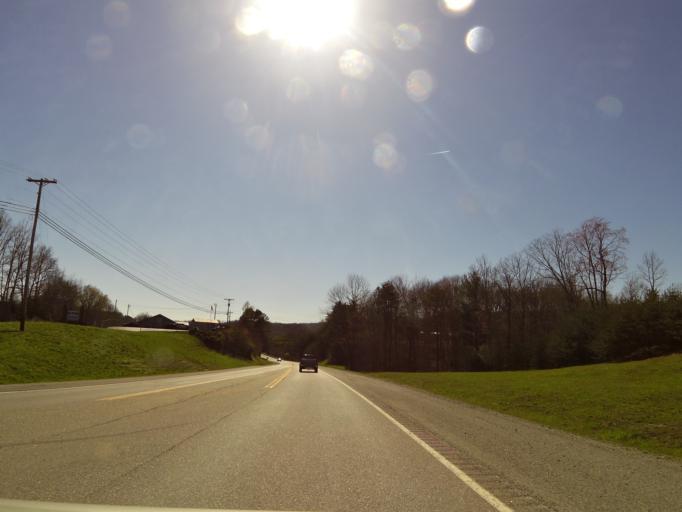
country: US
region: Tennessee
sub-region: Scott County
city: Oneida
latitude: 36.5363
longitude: -84.4820
